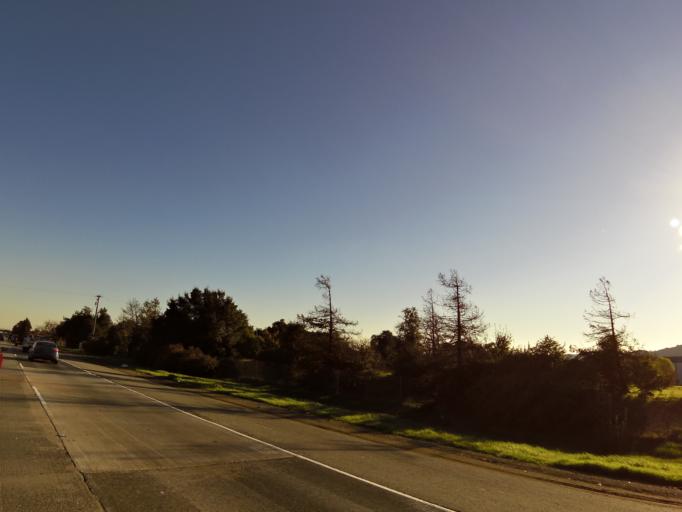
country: US
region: California
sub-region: Santa Clara County
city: Morgan Hill
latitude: 37.1463
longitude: -121.6463
